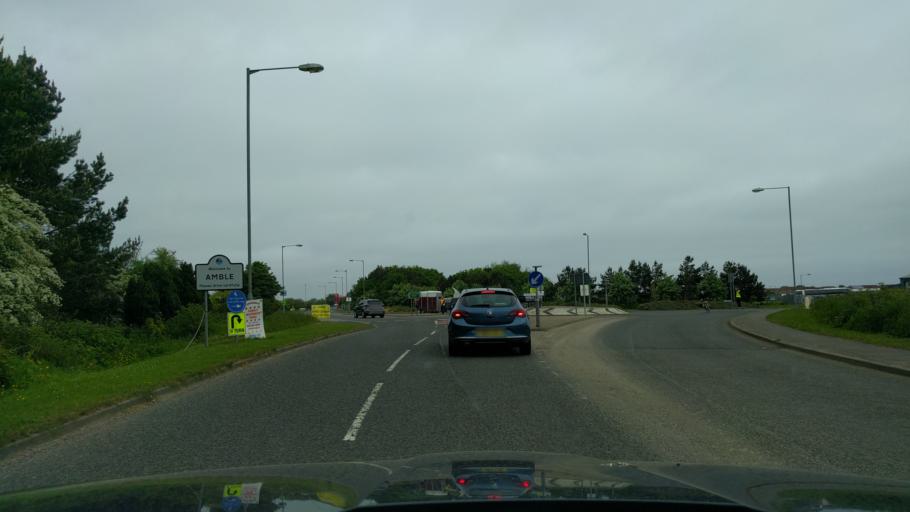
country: GB
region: England
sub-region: Northumberland
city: Amble
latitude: 55.3233
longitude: -1.5803
